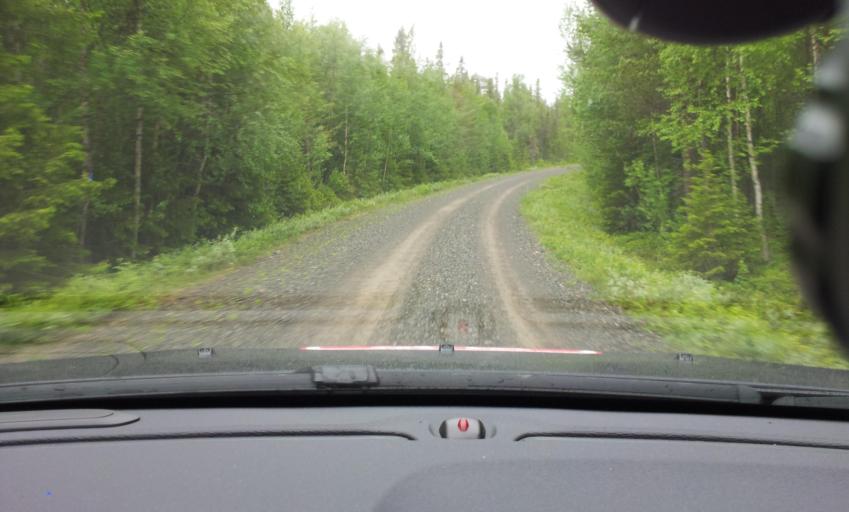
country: SE
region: Jaemtland
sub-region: Are Kommun
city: Jarpen
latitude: 63.1929
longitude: 13.2618
